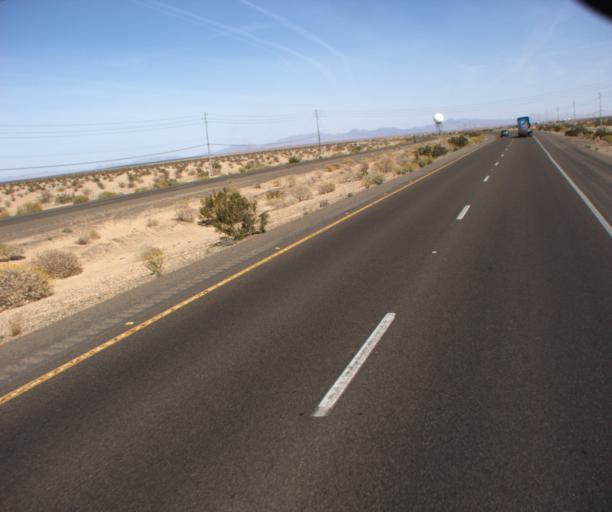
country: US
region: Arizona
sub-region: Yuma County
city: Somerton
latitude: 32.4945
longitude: -114.6646
